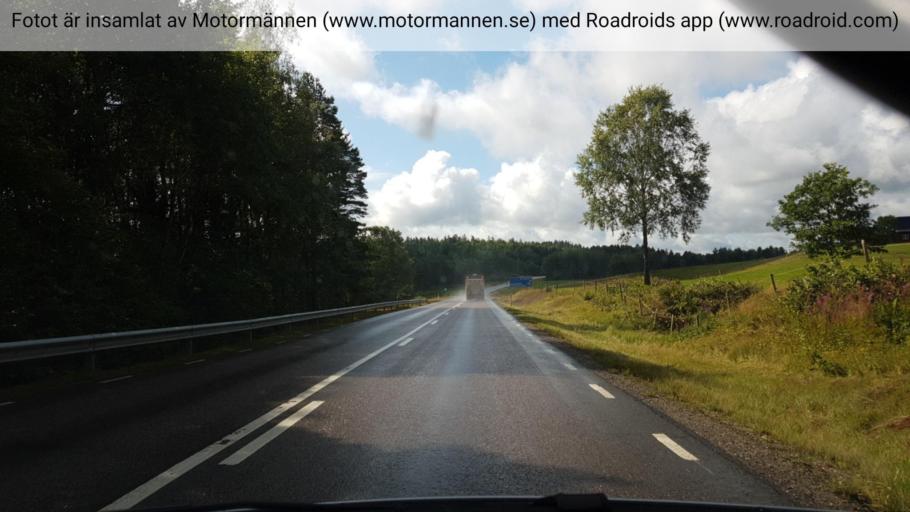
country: SE
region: Vaestra Goetaland
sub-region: Vargarda Kommun
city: Jonstorp
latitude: 58.0692
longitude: 12.6852
